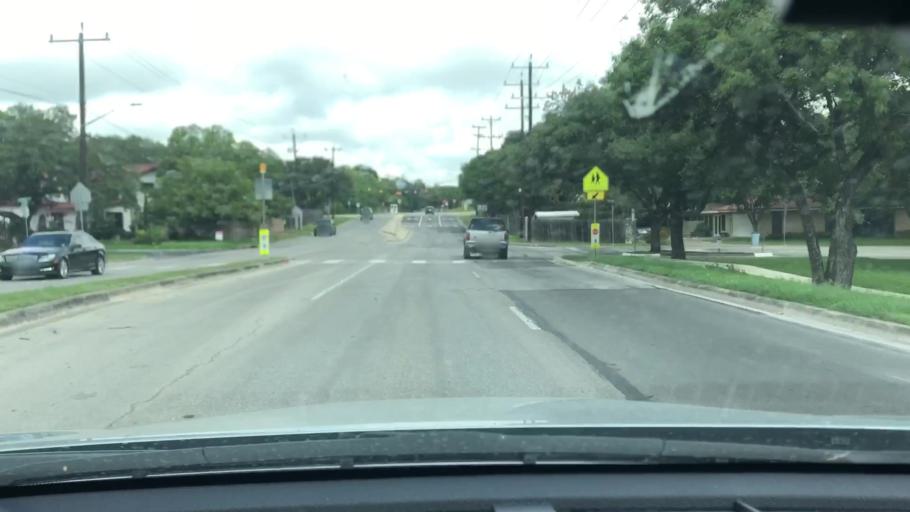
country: US
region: Texas
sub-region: Bexar County
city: Windcrest
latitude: 29.5181
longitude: -98.3695
